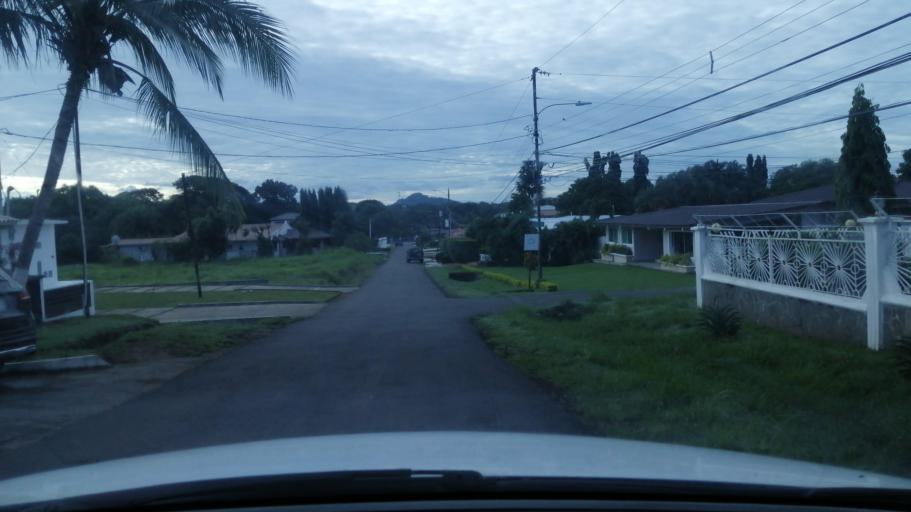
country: PA
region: Chiriqui
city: Mata del Nance
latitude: 8.4572
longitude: -82.4169
